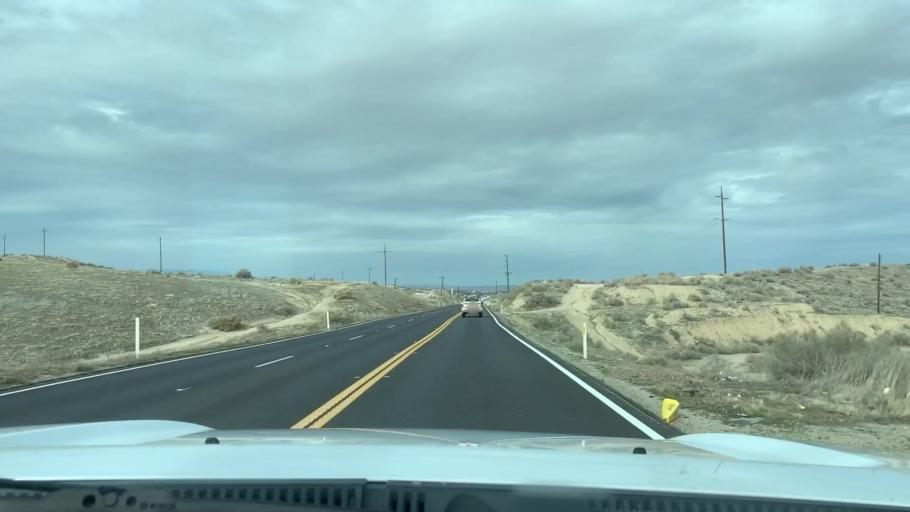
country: US
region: California
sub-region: Kern County
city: South Taft
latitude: 35.1207
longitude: -119.4349
